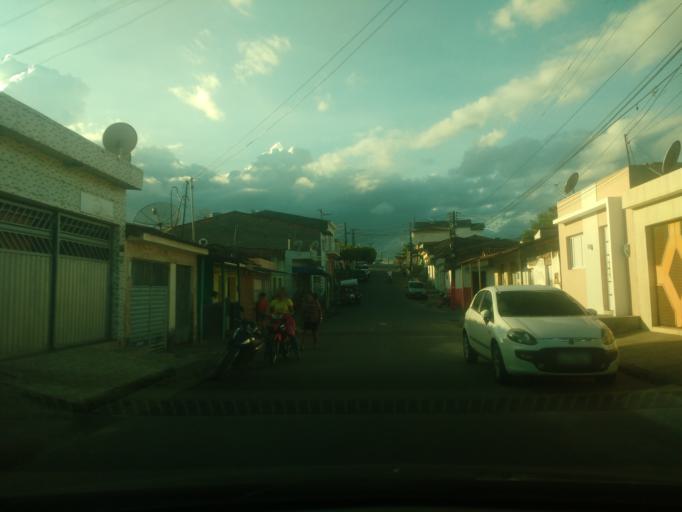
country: BR
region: Alagoas
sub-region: Uniao Dos Palmares
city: Uniao dos Palmares
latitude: -9.1607
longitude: -36.0284
